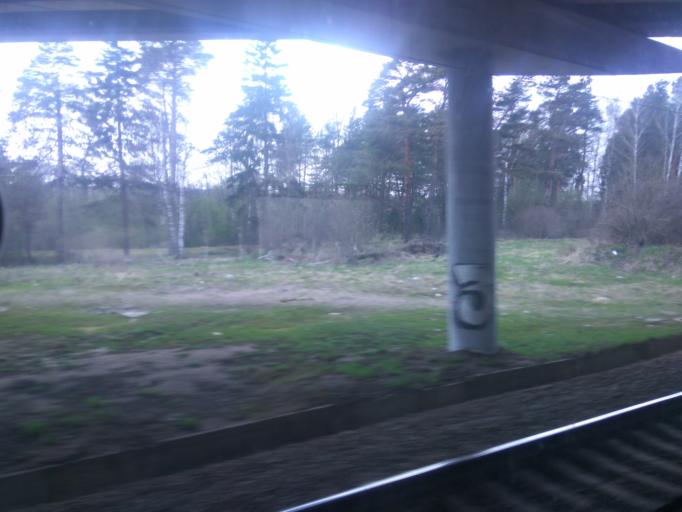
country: RU
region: Moskovskaya
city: Dedenevo
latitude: 56.2247
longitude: 37.5257
